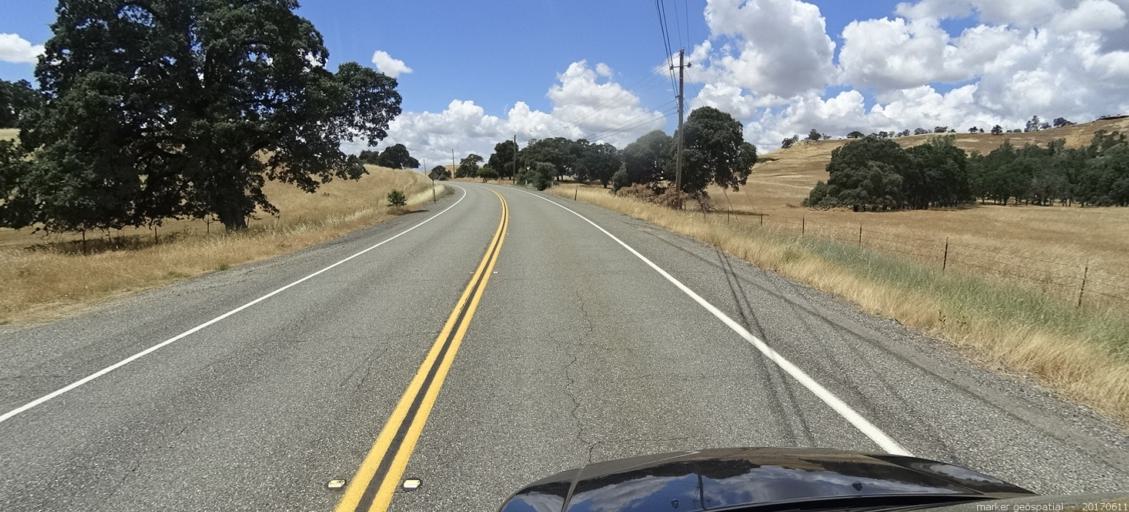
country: US
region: California
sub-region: Butte County
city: Paradise
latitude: 39.6532
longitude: -121.5932
